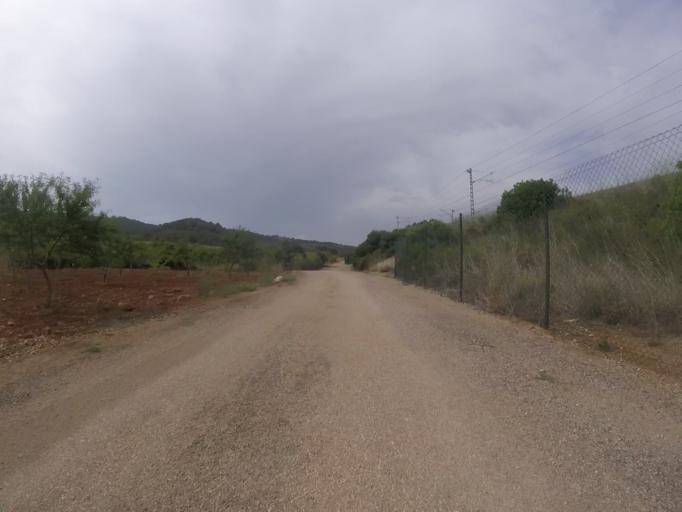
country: ES
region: Valencia
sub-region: Provincia de Castello
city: Alcoceber
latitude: 40.2622
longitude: 0.2552
